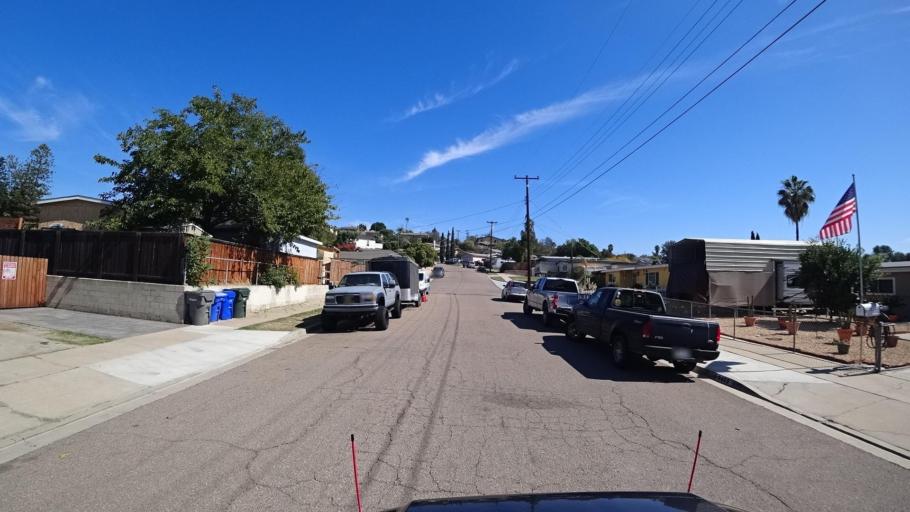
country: US
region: California
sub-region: San Diego County
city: La Presa
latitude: 32.7190
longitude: -117.0131
